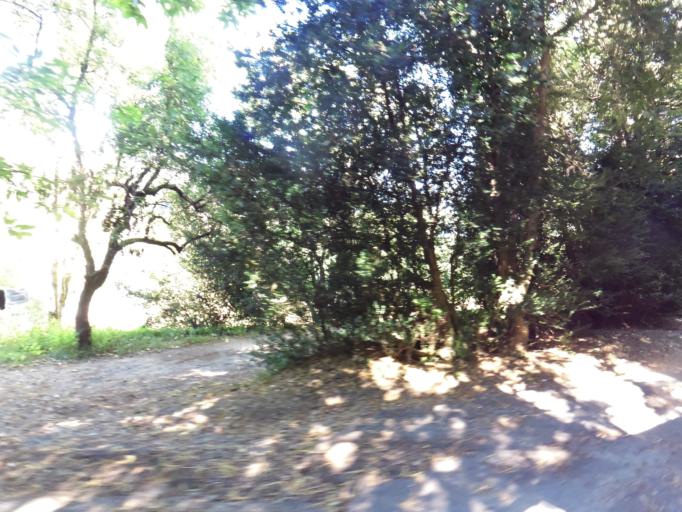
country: FR
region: Languedoc-Roussillon
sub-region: Departement du Gard
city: Saint-Jean-du-Gard
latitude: 44.1137
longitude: 3.8509
